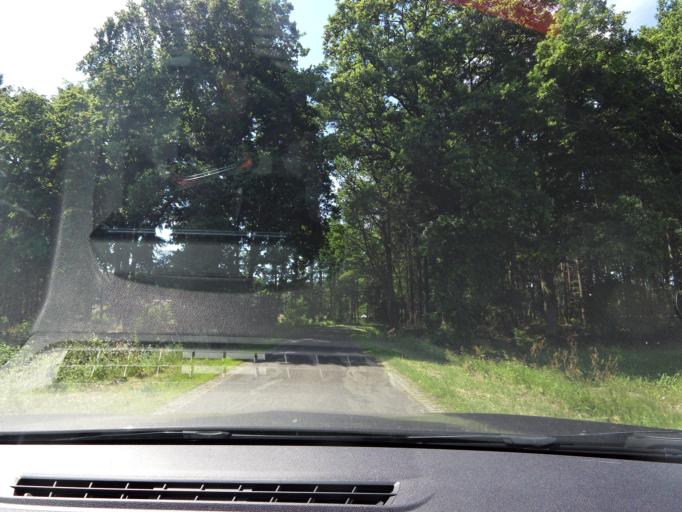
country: NL
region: Overijssel
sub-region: Gemeente Wierden
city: Wierden
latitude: 52.3242
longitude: 6.5468
